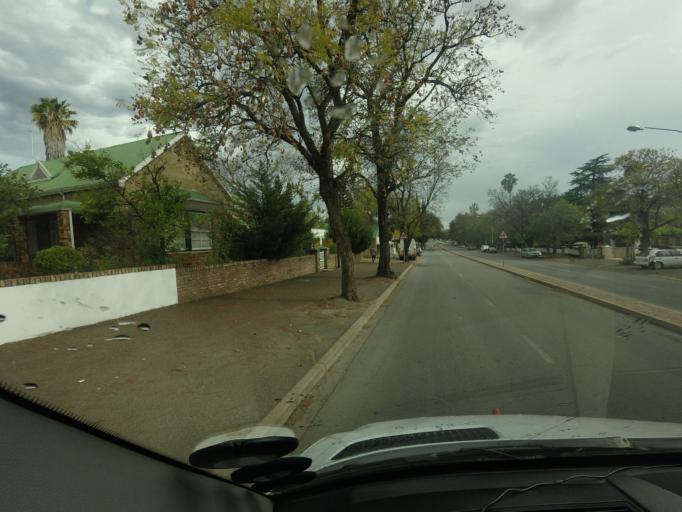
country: ZA
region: Western Cape
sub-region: Eden District Municipality
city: Oudtshoorn
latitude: -33.5844
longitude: 22.2043
